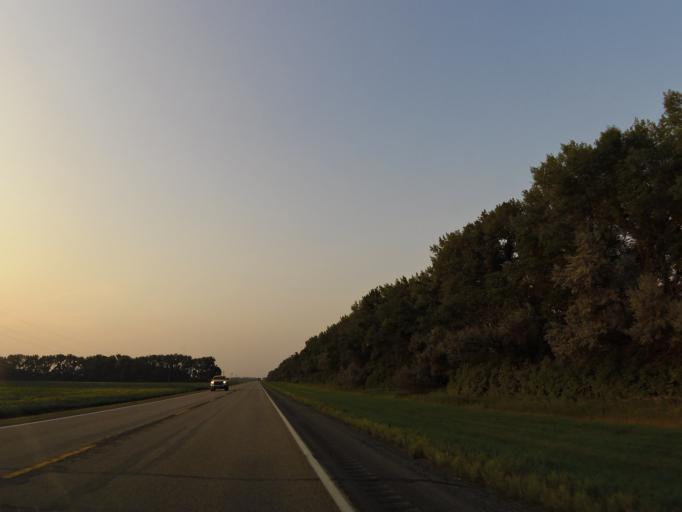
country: US
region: North Dakota
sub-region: Grand Forks County
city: Larimore
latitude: 47.9637
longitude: -97.6236
